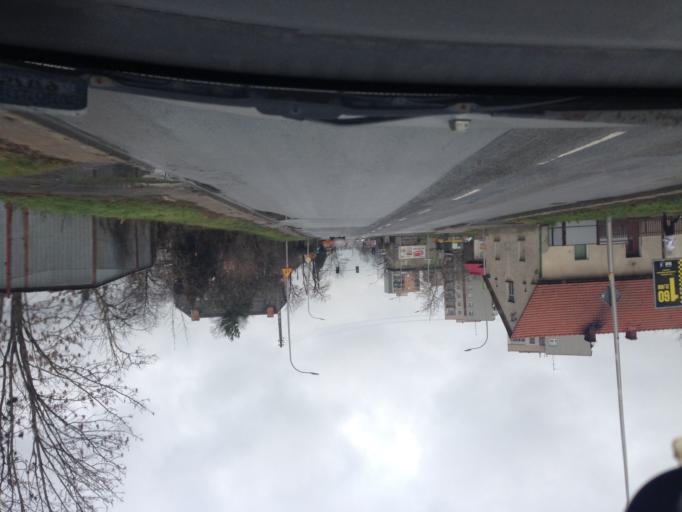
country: PL
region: Opole Voivodeship
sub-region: Powiat opolski
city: Opole
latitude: 50.6819
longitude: 17.9554
